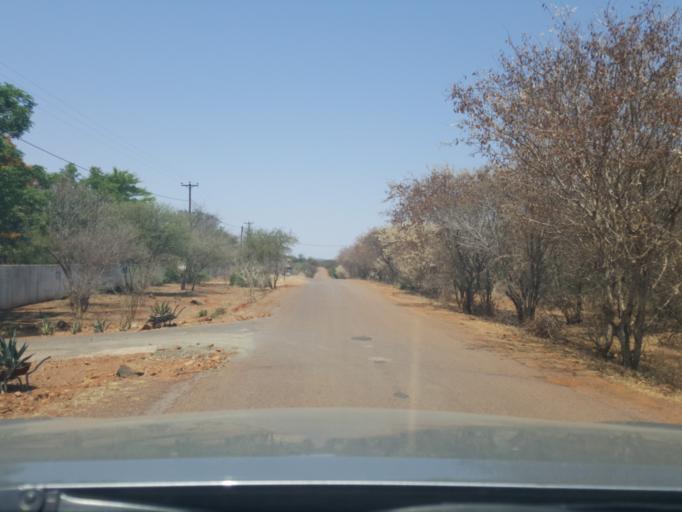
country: BW
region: South East
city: Ramotswa
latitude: -24.7665
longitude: 25.8454
